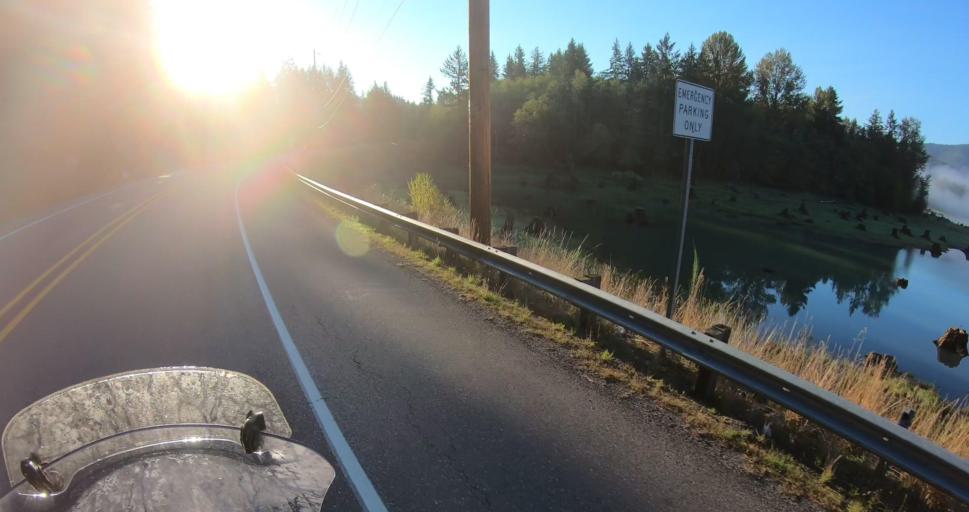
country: US
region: Washington
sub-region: Pierce County
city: Eatonville
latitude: 46.7951
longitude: -122.2744
